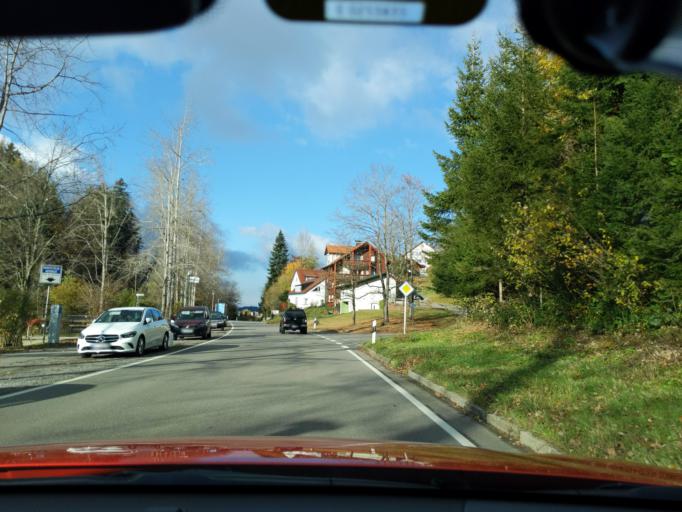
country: DE
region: Bavaria
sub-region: Swabia
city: Scheidegg
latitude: 47.5747
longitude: 9.8458
